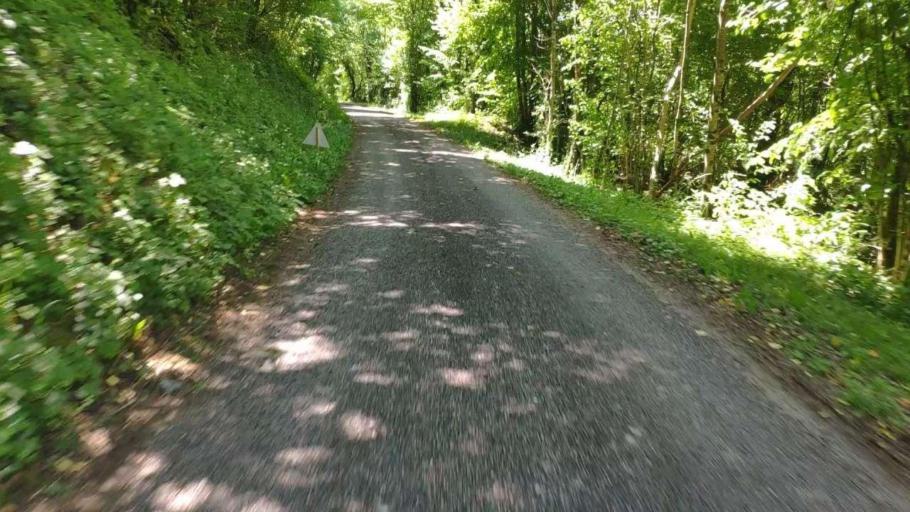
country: FR
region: Franche-Comte
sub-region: Departement du Jura
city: Poligny
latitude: 46.7548
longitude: 5.6754
